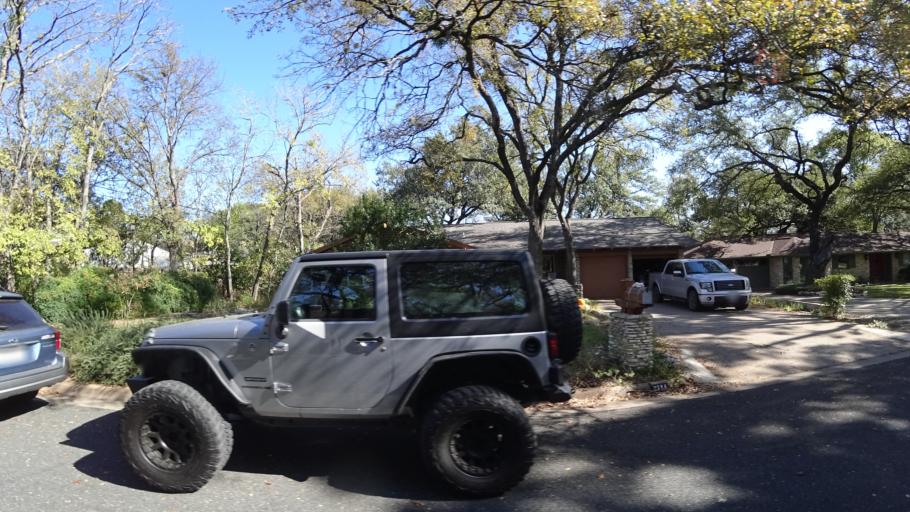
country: US
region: Texas
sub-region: Williamson County
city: Jollyville
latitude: 30.3772
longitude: -97.7420
